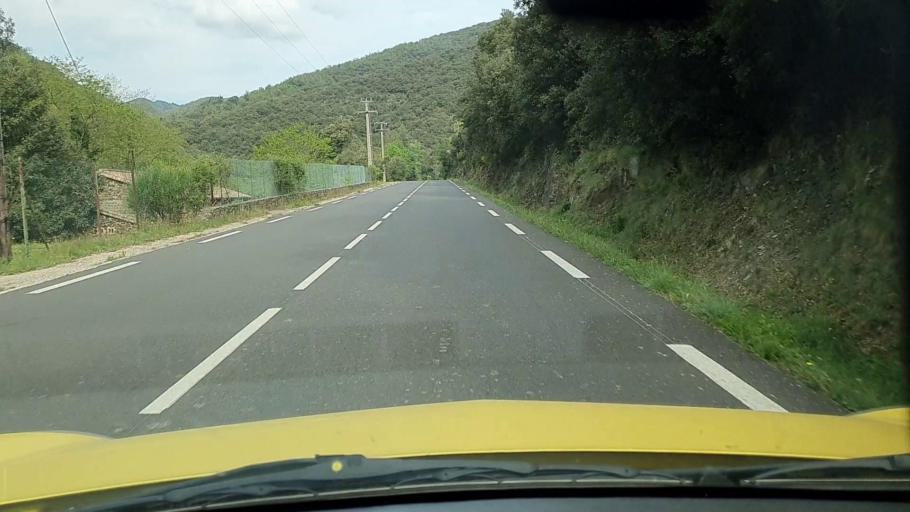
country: FR
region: Languedoc-Roussillon
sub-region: Departement du Gard
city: Valleraugue
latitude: 44.0756
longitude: 3.6686
